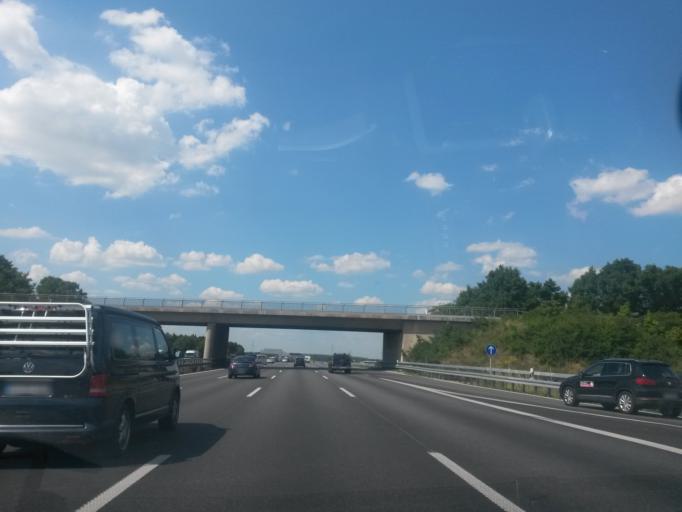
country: DE
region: Bavaria
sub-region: Upper Bavaria
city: Garching bei Munchen
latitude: 48.2635
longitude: 11.6469
